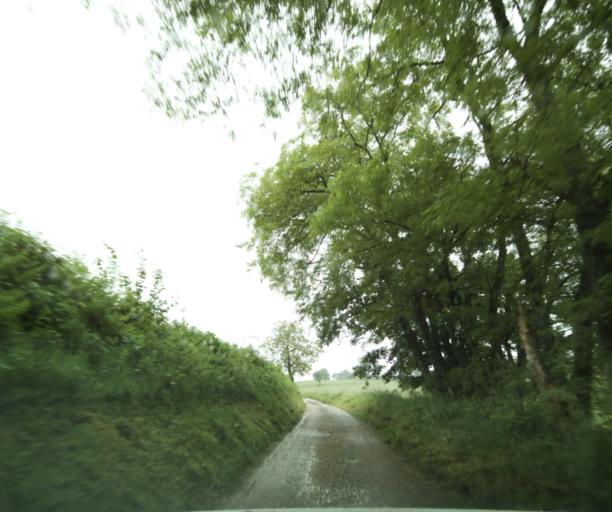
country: FR
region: Bourgogne
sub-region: Departement de Saone-et-Loire
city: Charolles
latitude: 46.4072
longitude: 4.3873
